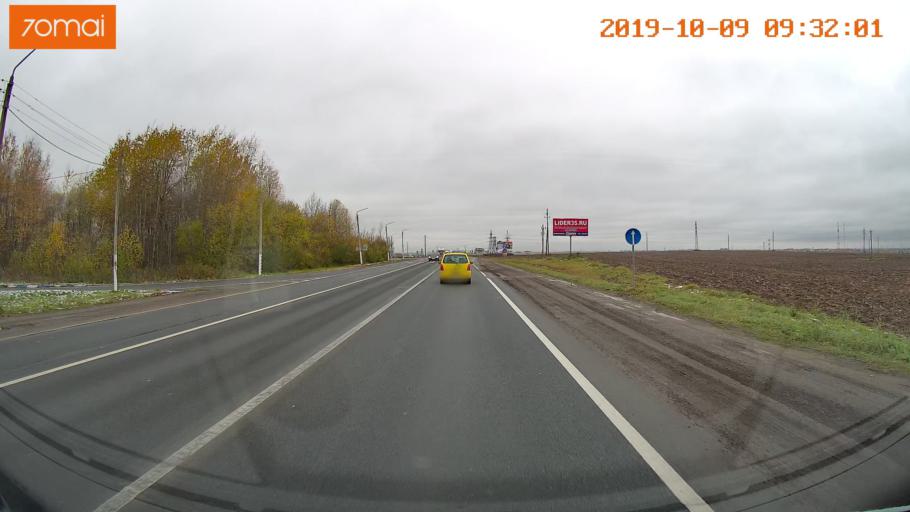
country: RU
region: Vologda
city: Vologda
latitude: 59.1546
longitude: 39.9331
